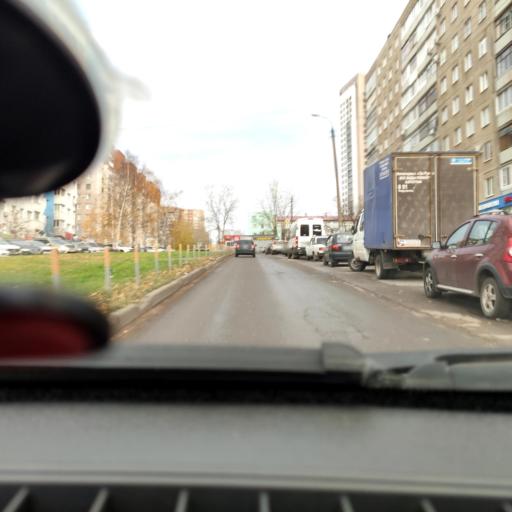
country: RU
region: Bashkortostan
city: Ufa
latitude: 54.7343
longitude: 55.9943
